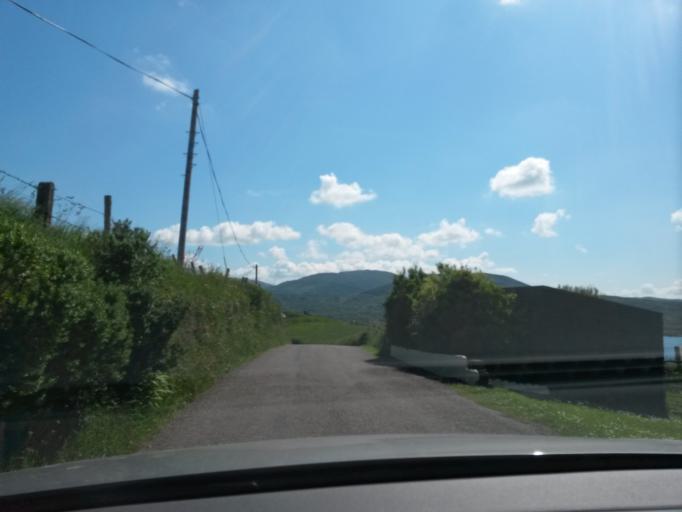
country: IE
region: Munster
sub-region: Ciarrai
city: Cahersiveen
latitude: 51.7154
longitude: -9.9713
